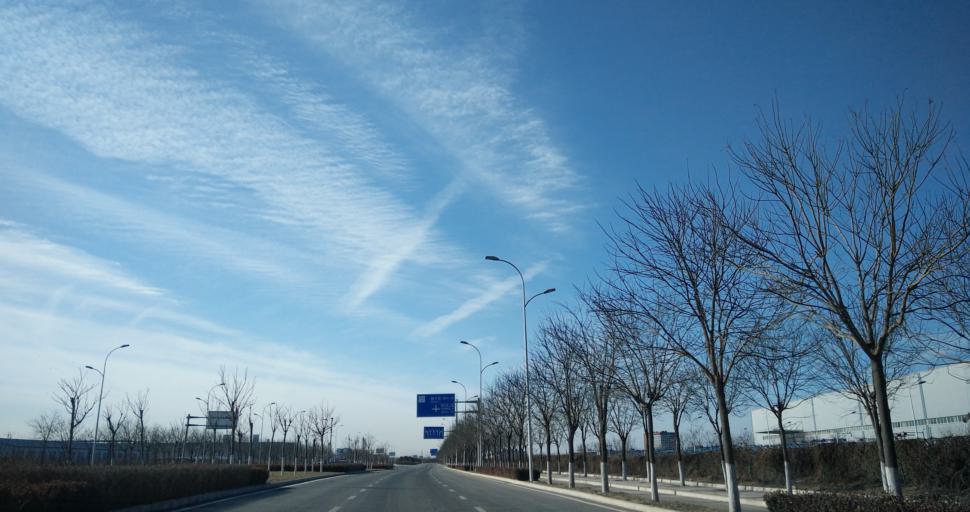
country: CN
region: Beijing
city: Qingyundian
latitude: 39.7245
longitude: 116.5158
